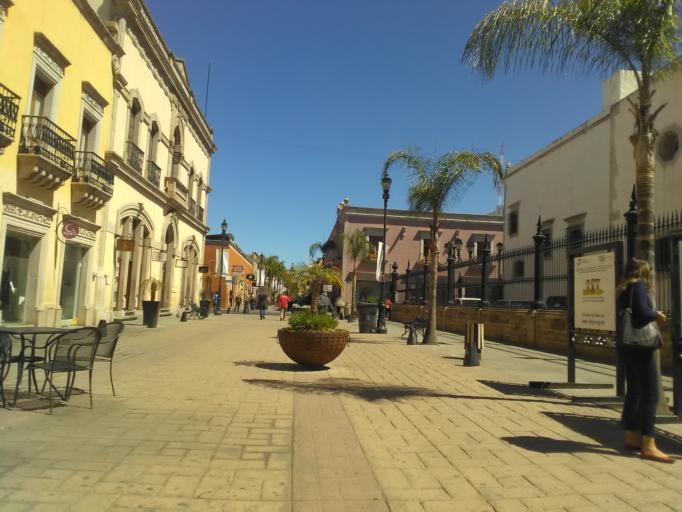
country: MX
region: Durango
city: Victoria de Durango
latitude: 24.0259
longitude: -104.6705
